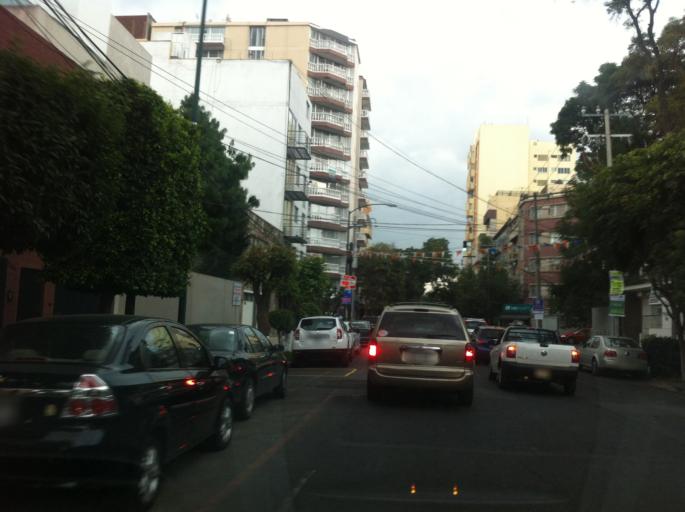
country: MX
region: Mexico City
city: Colonia del Valle
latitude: 19.3784
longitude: -99.1647
